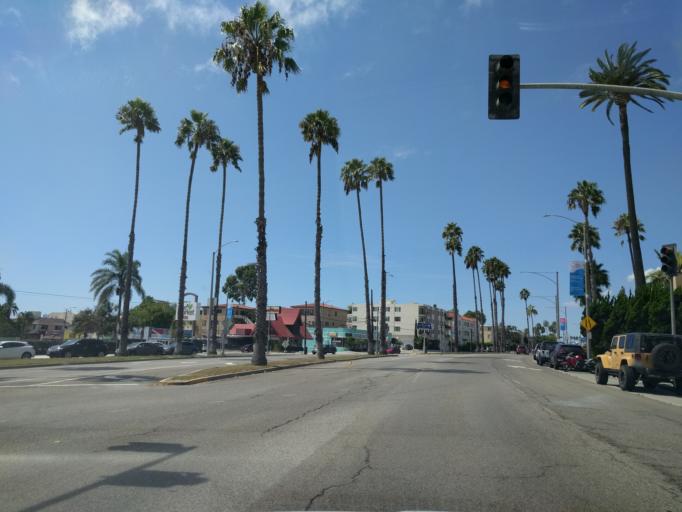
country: US
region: California
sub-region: Los Angeles County
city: Long Beach
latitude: 33.7605
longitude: -118.1470
